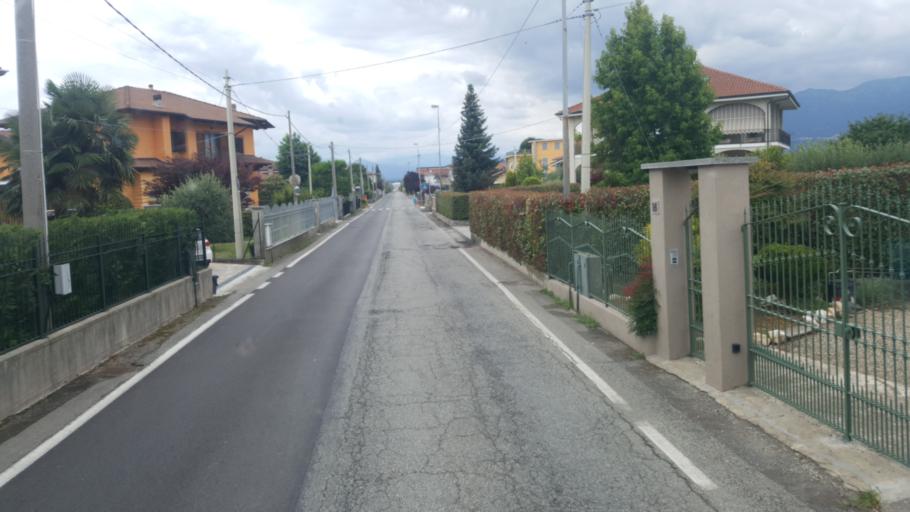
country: IT
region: Piedmont
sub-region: Provincia di Torino
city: Salassa
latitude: 45.3558
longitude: 7.6872
